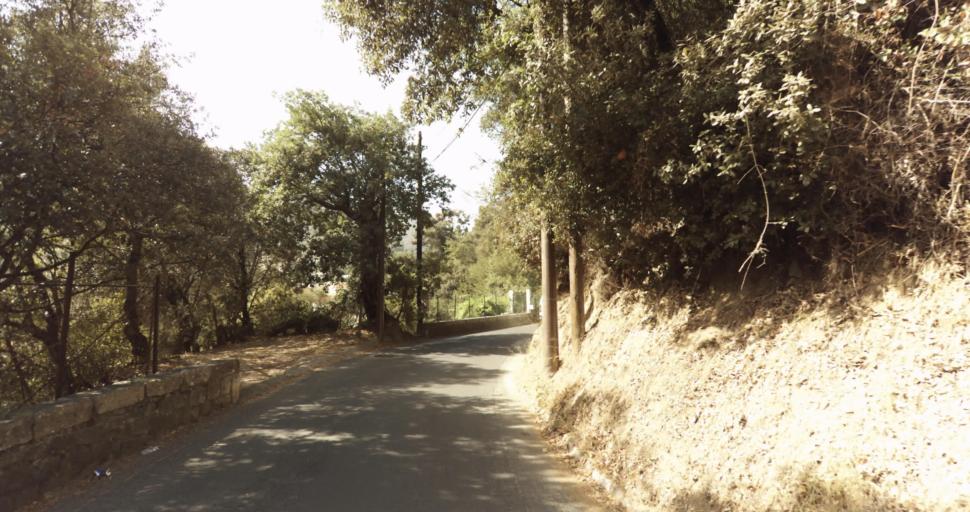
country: FR
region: Provence-Alpes-Cote d'Azur
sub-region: Departement des Alpes-Maritimes
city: Sainte-Agnes
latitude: 43.7911
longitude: 7.4807
